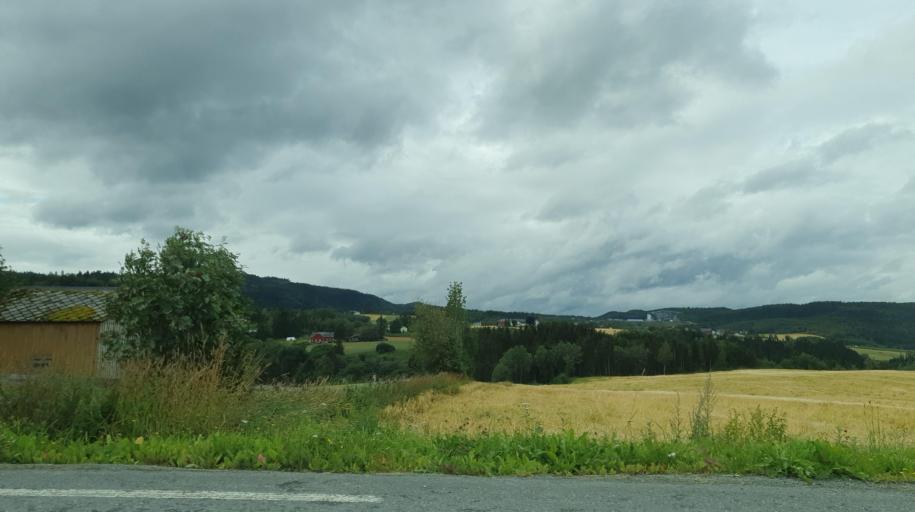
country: NO
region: Nord-Trondelag
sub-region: Stjordal
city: Stjordalshalsen
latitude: 63.4148
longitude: 10.9603
